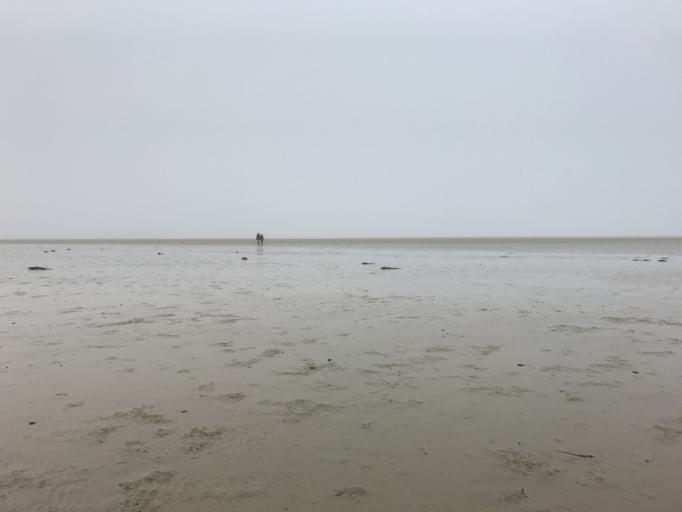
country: DE
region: Lower Saxony
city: Borkum
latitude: 53.5965
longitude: 6.6524
